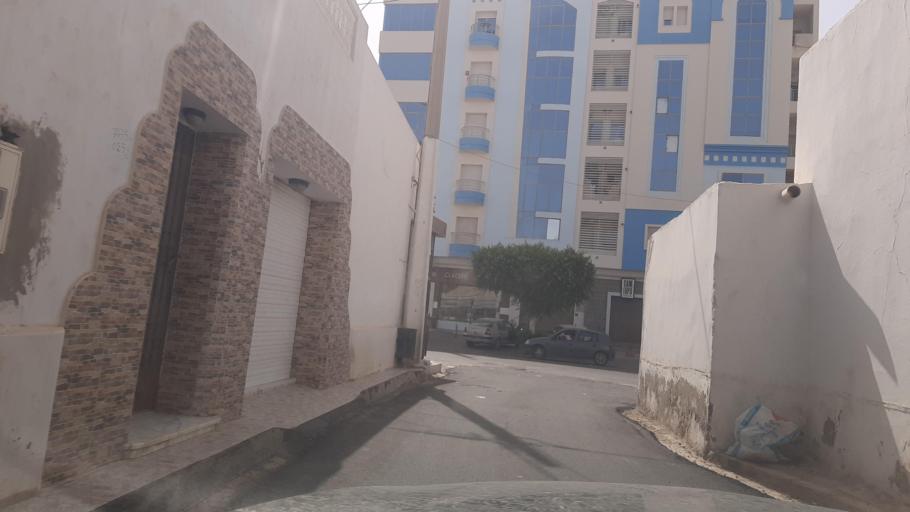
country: TN
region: Safaqis
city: Sfax
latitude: 34.7586
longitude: 10.7563
